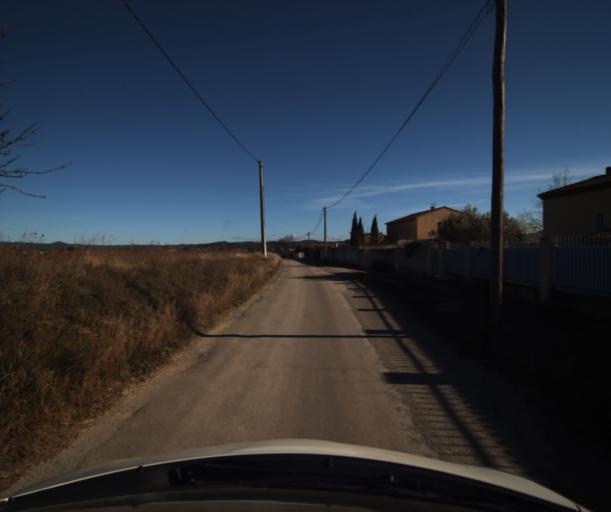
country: FR
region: Provence-Alpes-Cote d'Azur
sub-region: Departement du Vaucluse
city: Pertuis
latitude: 43.7009
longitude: 5.4857
